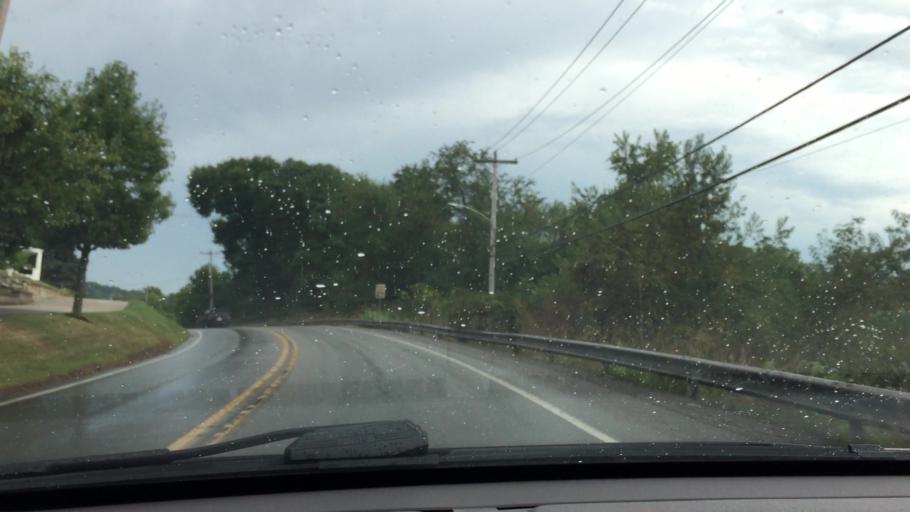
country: US
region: Pennsylvania
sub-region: Washington County
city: Canonsburg
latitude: 40.2721
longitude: -80.1879
